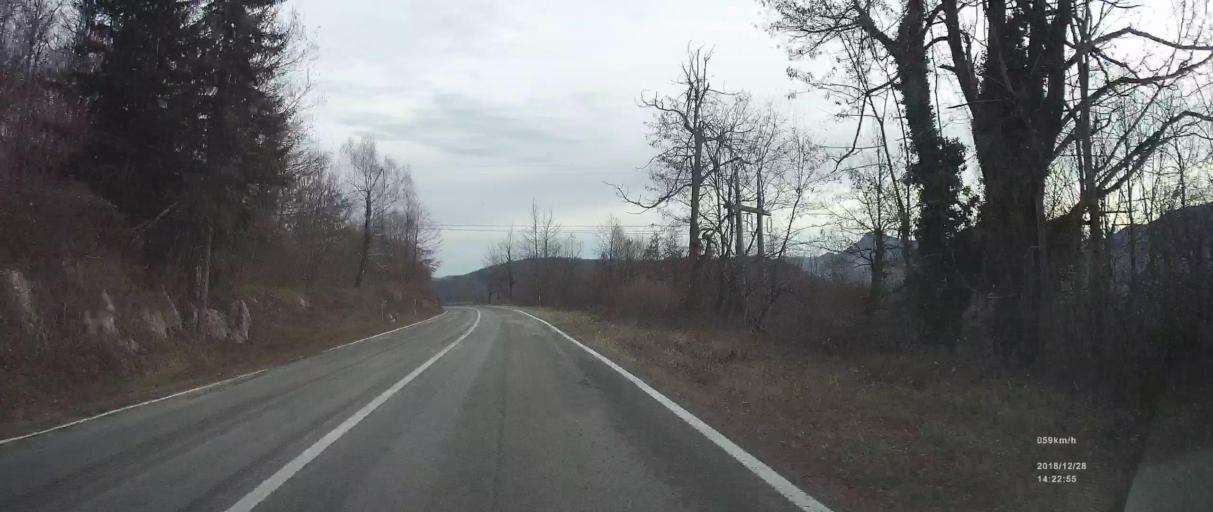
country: HR
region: Primorsko-Goranska
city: Vrbovsko
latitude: 45.3815
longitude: 15.0892
